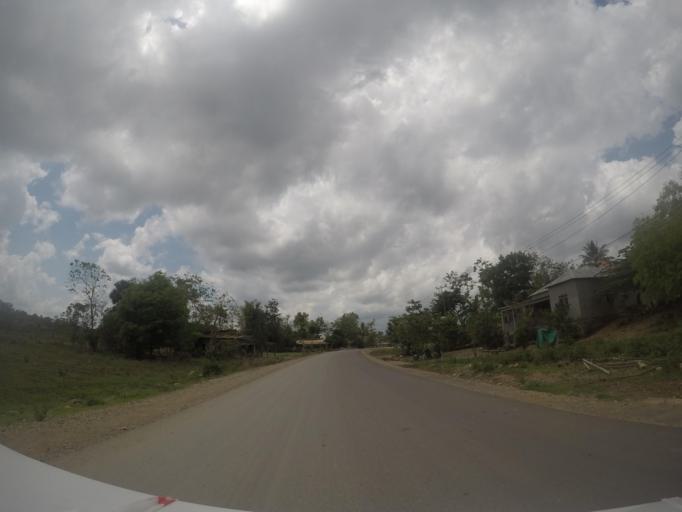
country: TL
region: Baucau
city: Baucau
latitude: -8.5363
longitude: 126.4197
